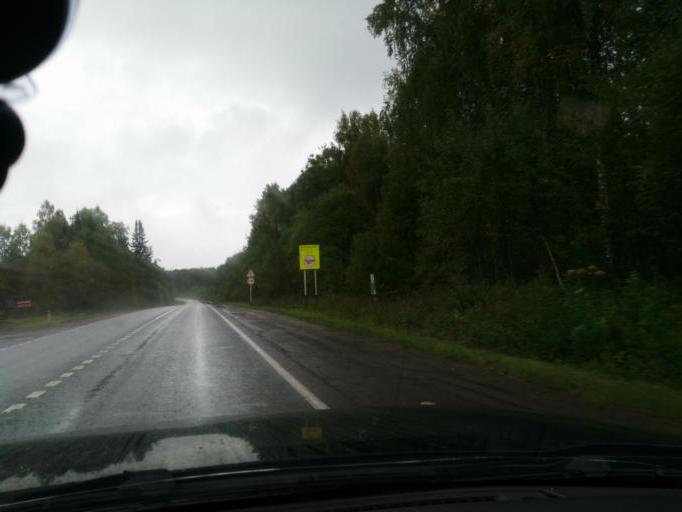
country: RU
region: Perm
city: Yugo-Kamskiy
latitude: 57.7385
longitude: 55.7102
